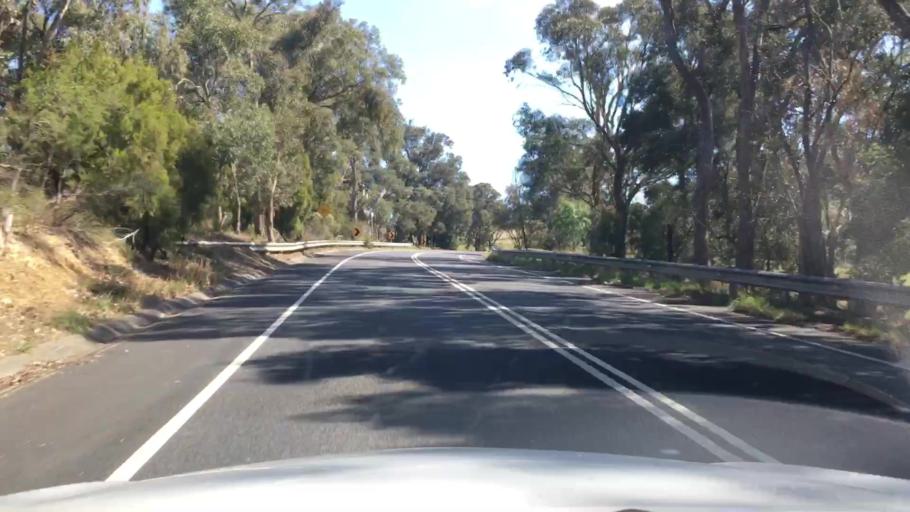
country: AU
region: Victoria
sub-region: Nillumbik
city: North Warrandyte
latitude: -37.6808
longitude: 145.2418
